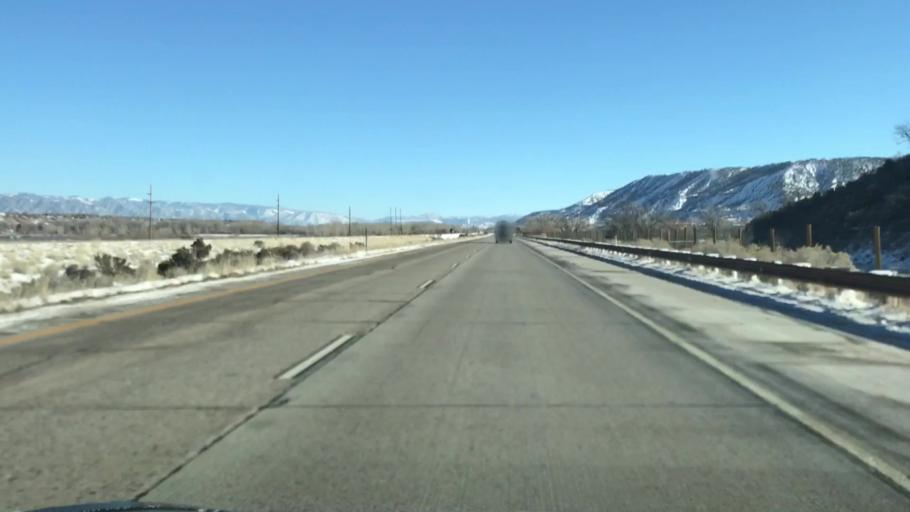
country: US
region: Colorado
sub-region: Garfield County
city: Rifle
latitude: 39.5197
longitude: -107.8202
